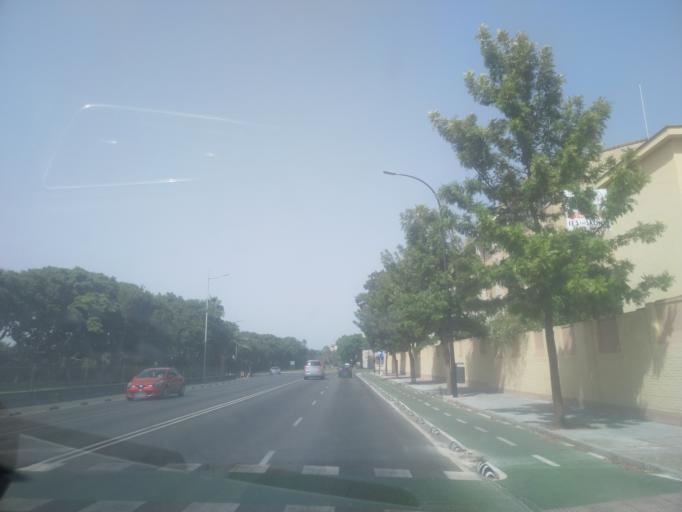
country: ES
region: Andalusia
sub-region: Provincia de Cadiz
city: San Fernando
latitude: 36.4586
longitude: -6.2125
